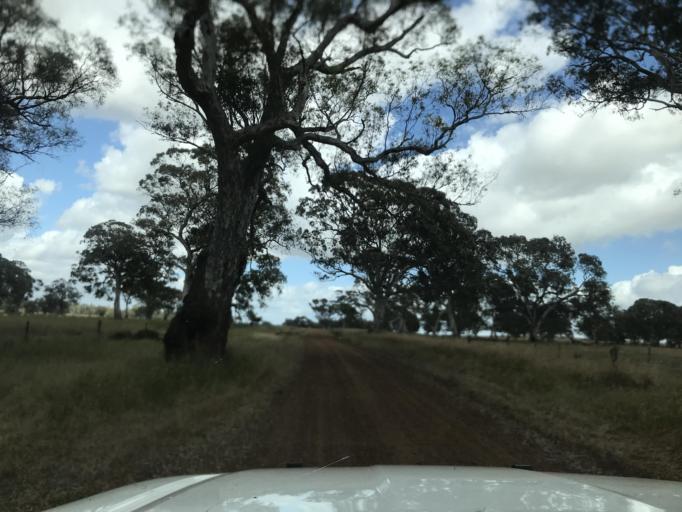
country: AU
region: South Australia
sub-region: Wattle Range
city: Penola
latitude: -37.1902
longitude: 141.4346
